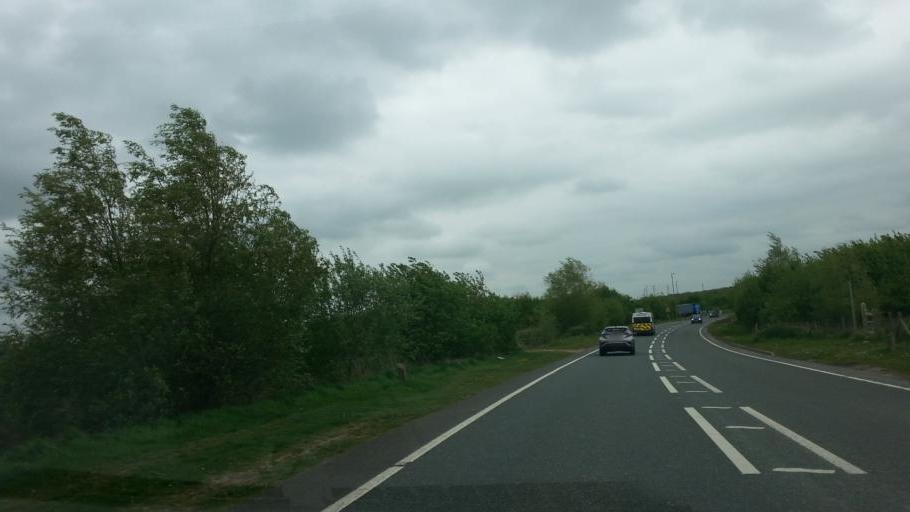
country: GB
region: England
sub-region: Lincolnshire
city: Bourne
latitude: 52.7574
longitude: -0.3902
